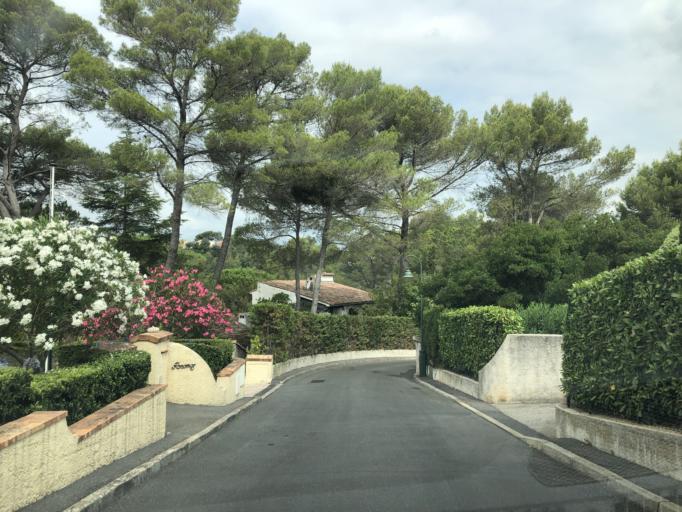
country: FR
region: Provence-Alpes-Cote d'Azur
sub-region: Departement des Alpes-Maritimes
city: Biot
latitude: 43.6271
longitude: 7.0819
